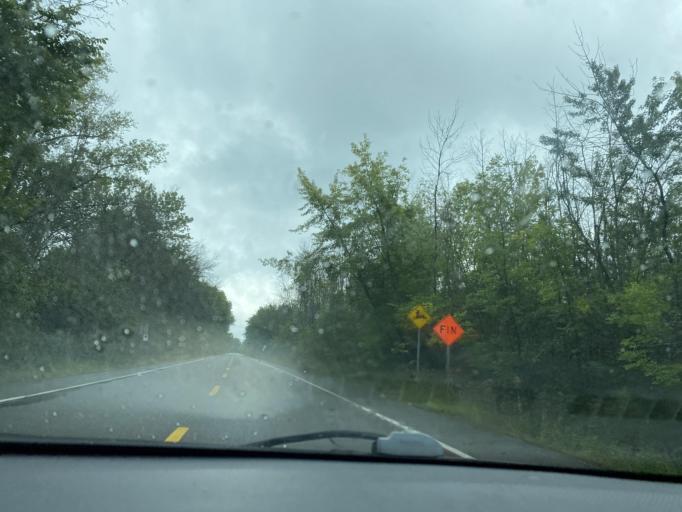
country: CA
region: Quebec
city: Baie-D'Urfe
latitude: 45.4491
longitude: -73.9345
